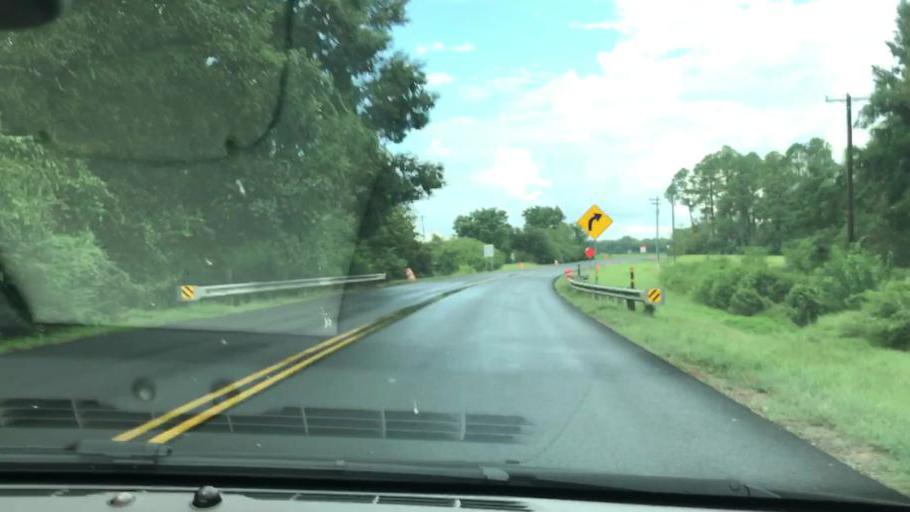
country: US
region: Georgia
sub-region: Early County
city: Blakely
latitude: 31.4008
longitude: -84.9590
